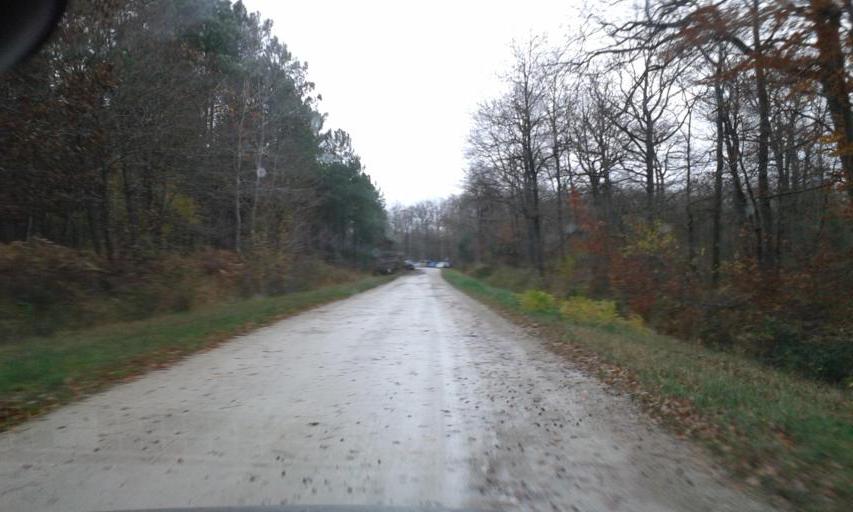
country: FR
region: Centre
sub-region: Departement du Loiret
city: Vitry-aux-Loges
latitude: 47.9856
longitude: 2.2996
